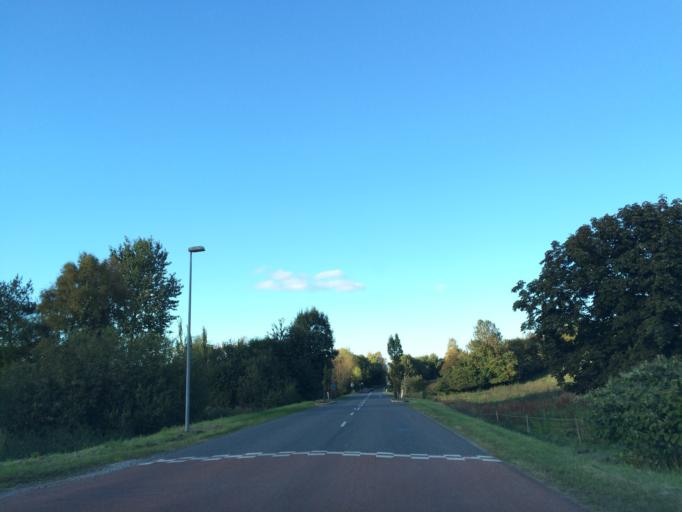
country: DK
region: Central Jutland
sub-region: Skanderborg Kommune
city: Ry
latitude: 56.1119
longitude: 9.7341
